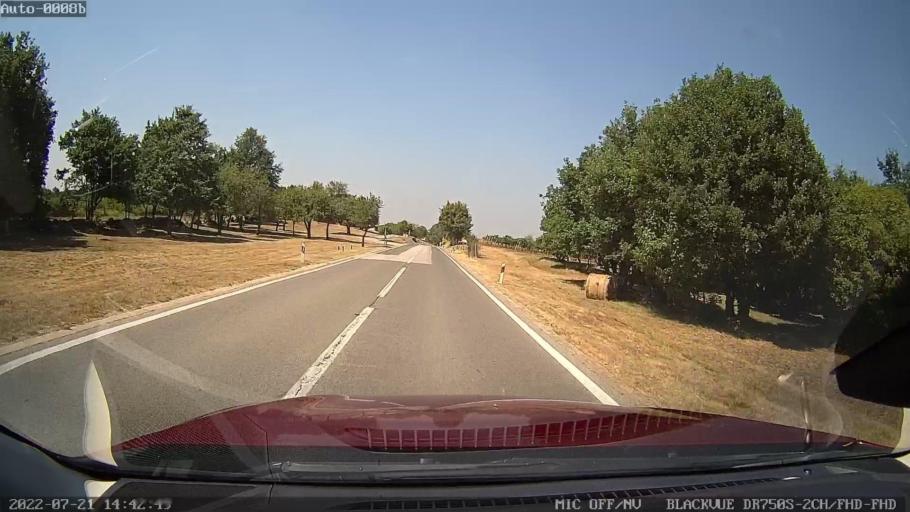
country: HR
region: Istarska
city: Vodnjan
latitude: 45.1026
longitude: 13.8834
